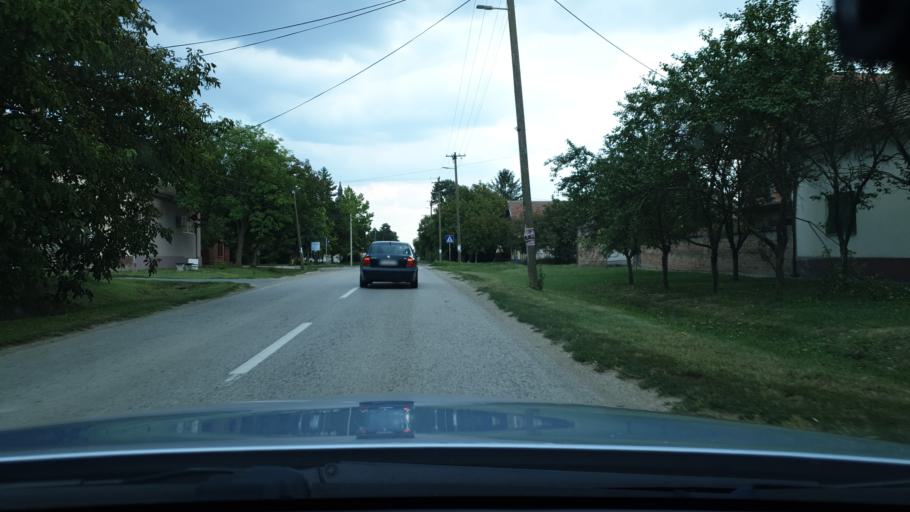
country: RS
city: Konak
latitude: 45.3145
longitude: 20.9087
